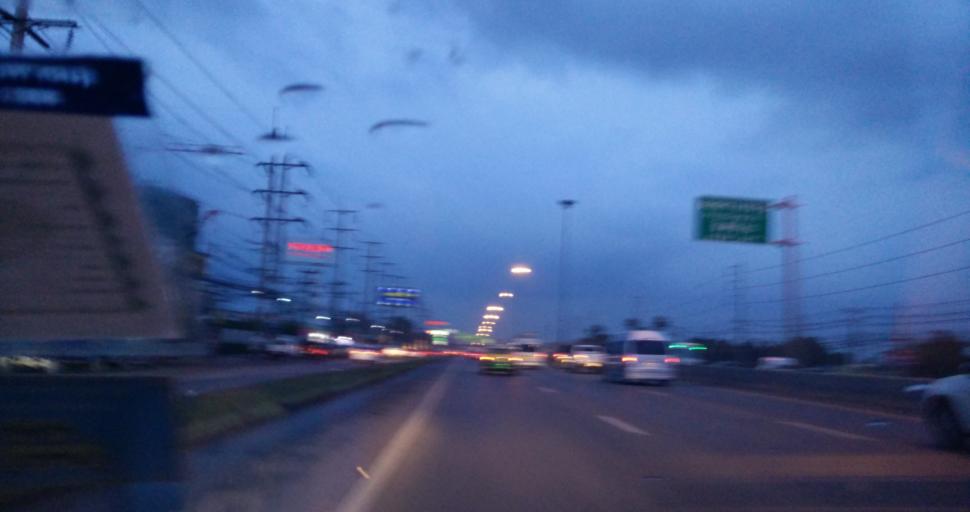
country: TH
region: Pathum Thani
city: Khlong Luang
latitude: 14.0199
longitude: 100.6155
